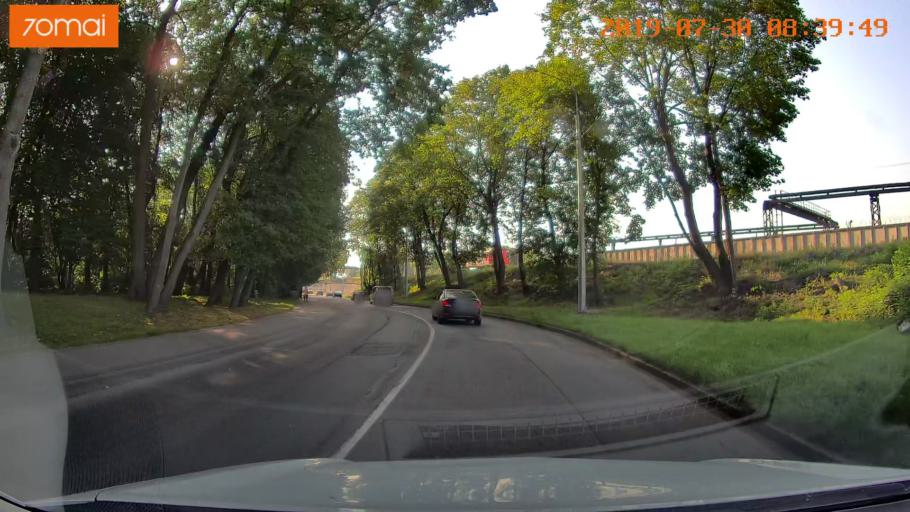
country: RU
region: Kaliningrad
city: Chernyakhovsk
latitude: 54.6306
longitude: 21.8068
